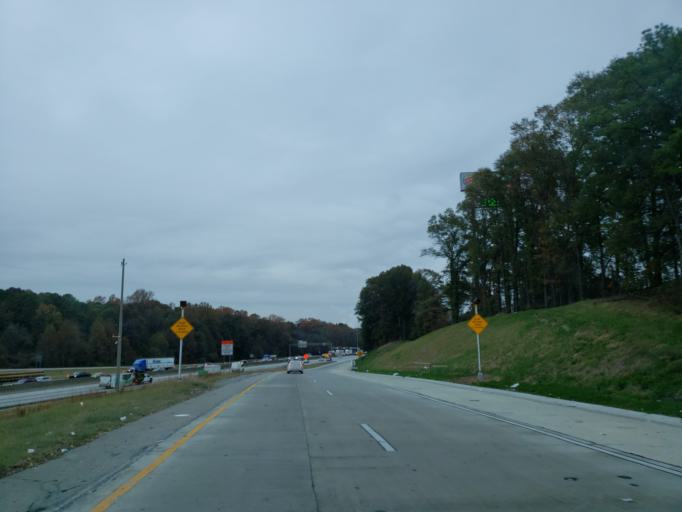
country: US
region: Georgia
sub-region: Cobb County
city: Vinings
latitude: 33.7867
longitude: -84.4922
